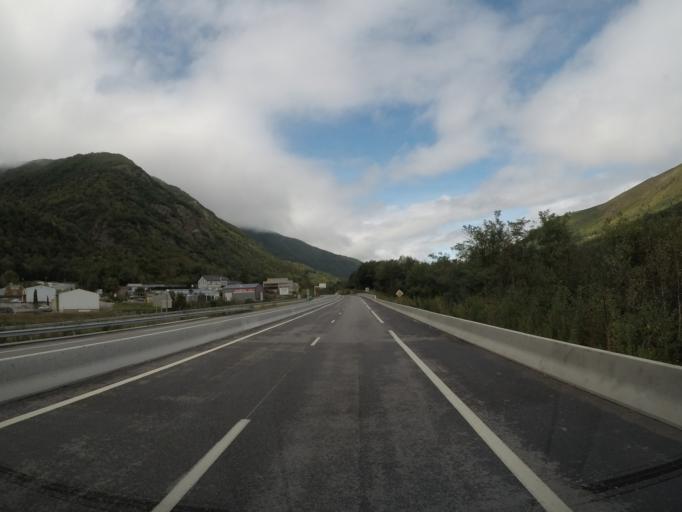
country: FR
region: Midi-Pyrenees
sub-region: Departement de l'Ariege
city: Ax-les-Thermes
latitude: 42.7310
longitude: 1.8027
